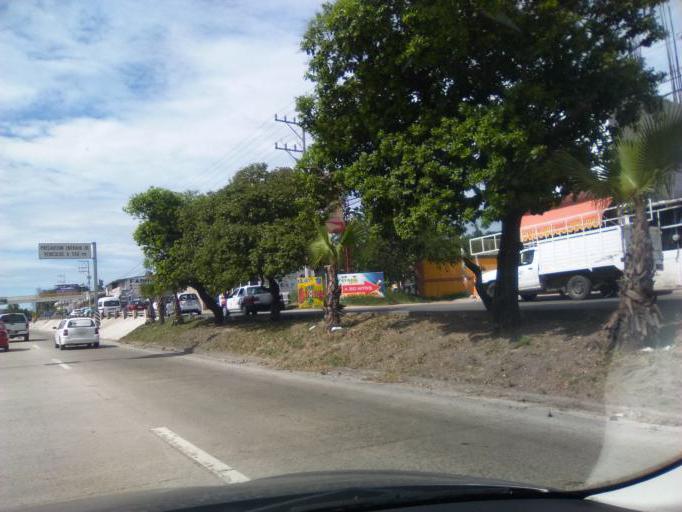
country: MX
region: Guerrero
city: Chilpancingo de los Bravos
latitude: 17.5214
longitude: -99.4850
